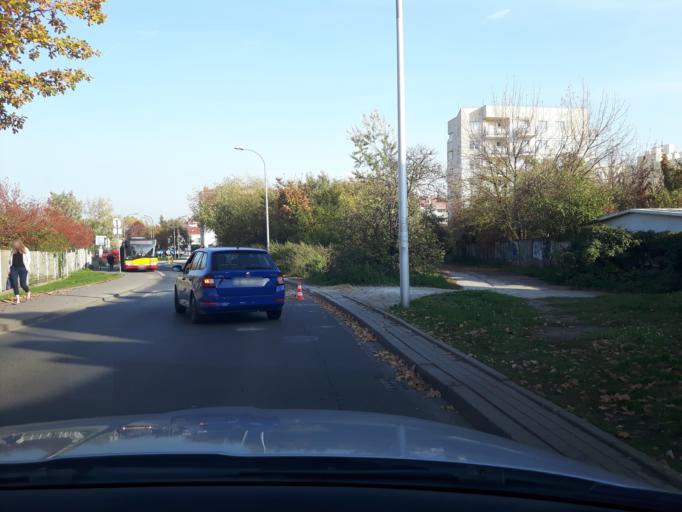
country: PL
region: Masovian Voivodeship
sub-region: Warszawa
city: Ochota
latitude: 52.2111
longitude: 20.9596
